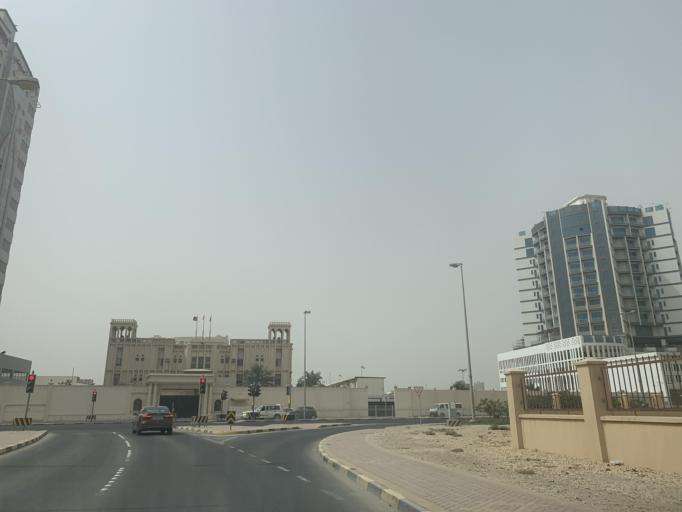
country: BH
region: Manama
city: Jidd Hafs
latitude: 26.2285
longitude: 50.5404
